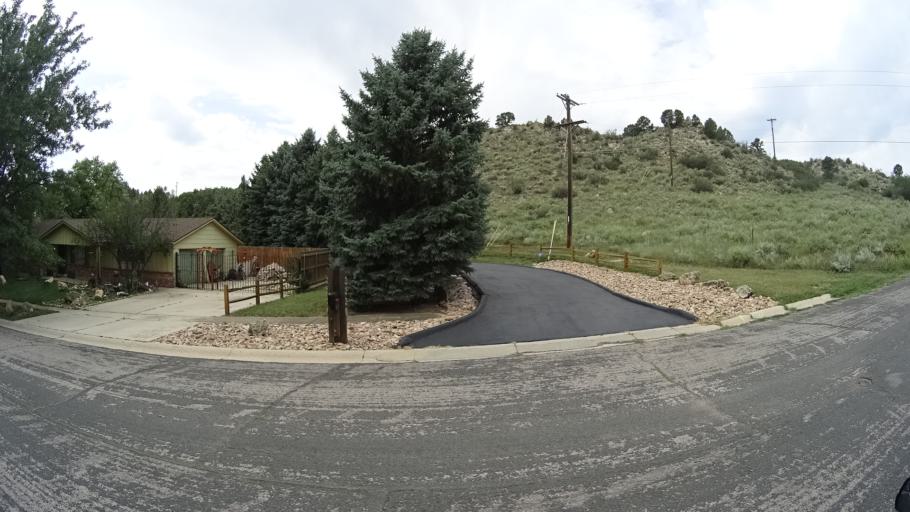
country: US
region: Colorado
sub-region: El Paso County
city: Manitou Springs
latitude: 38.8627
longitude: -104.8727
